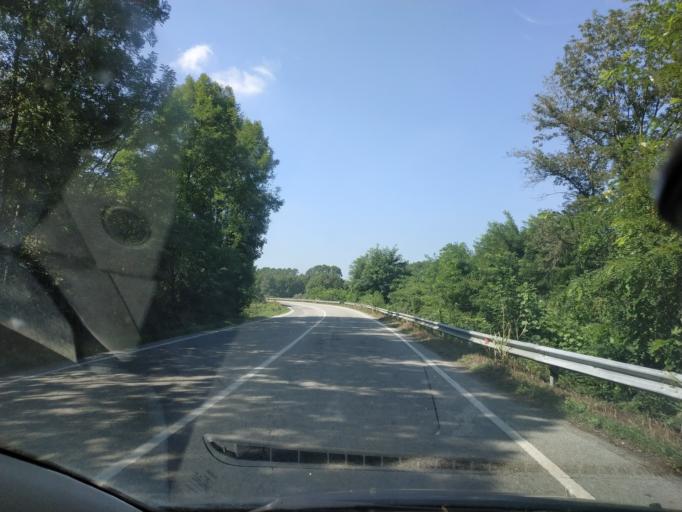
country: IT
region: Piedmont
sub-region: Provincia di Torino
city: San Benigno Canavese
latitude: 45.2442
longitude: 7.8010
